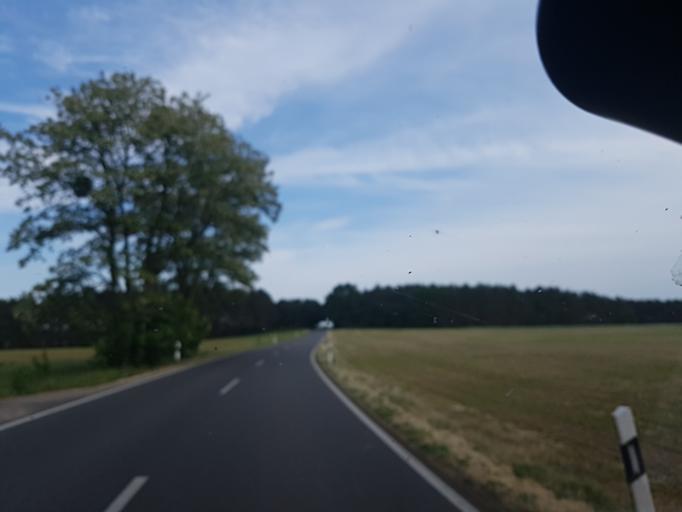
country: DE
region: Saxony-Anhalt
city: Zahna
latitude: 51.9303
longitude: 12.7717
